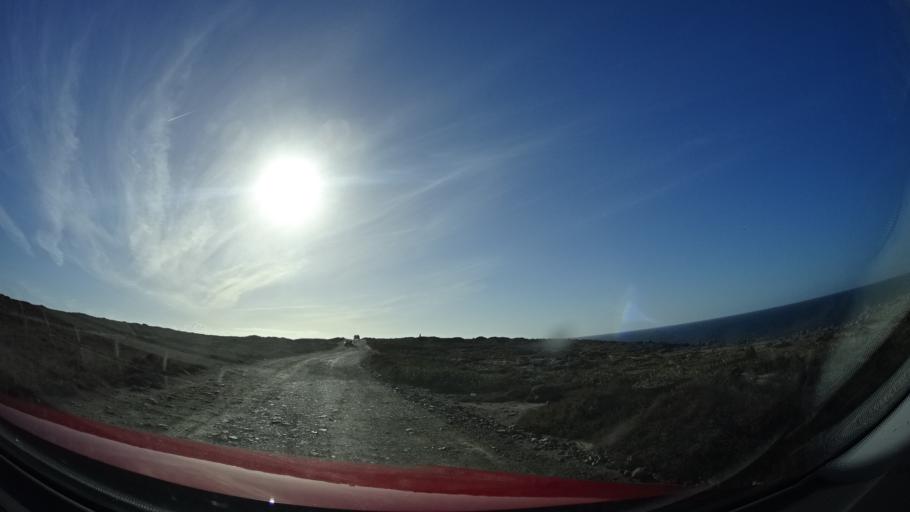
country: PT
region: Faro
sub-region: Vila do Bispo
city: Vila do Bispo
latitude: 37.1962
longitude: -8.9143
